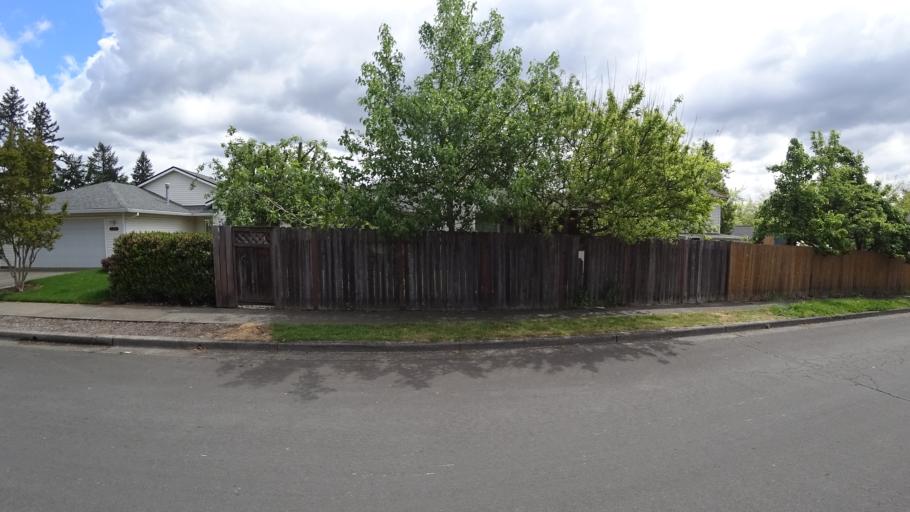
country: US
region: Oregon
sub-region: Washington County
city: Beaverton
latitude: 45.4683
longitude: -122.7988
